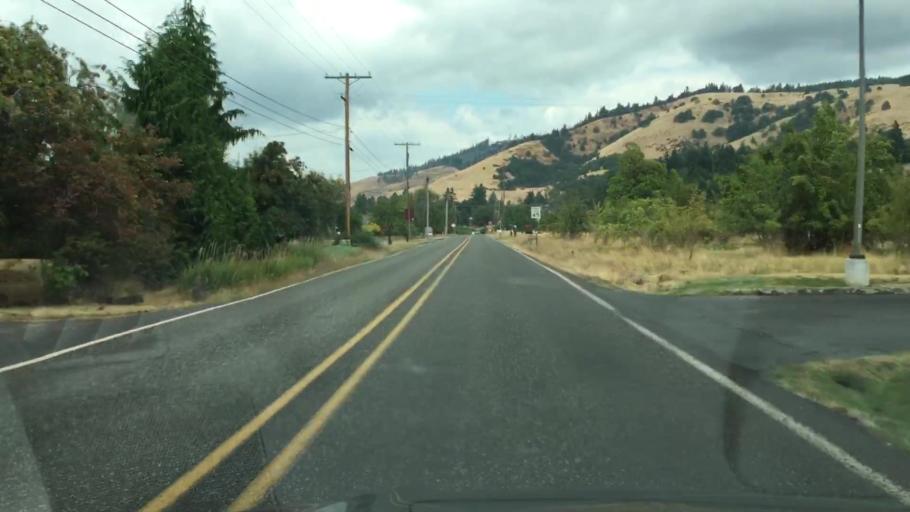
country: US
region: Washington
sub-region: Klickitat County
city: White Salmon
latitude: 45.7361
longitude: -121.5124
